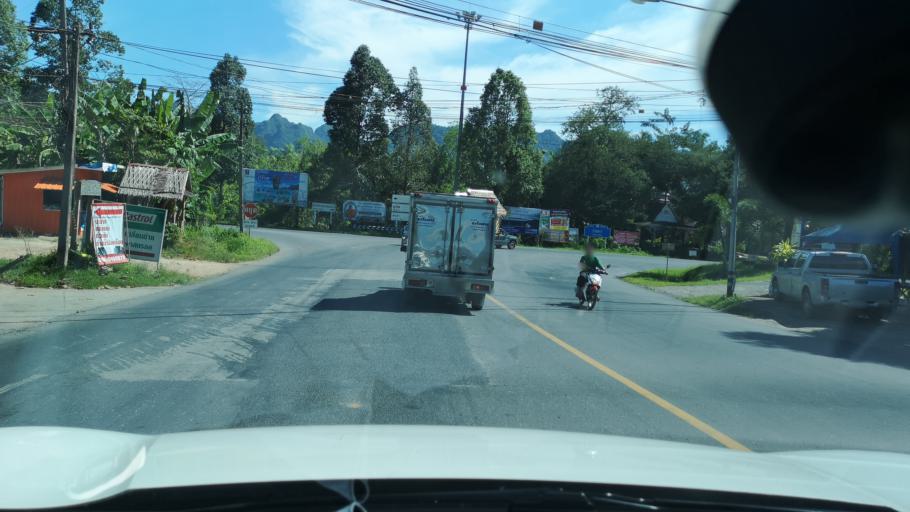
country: TH
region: Phangnga
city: Phang Nga
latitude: 8.5258
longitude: 98.5195
